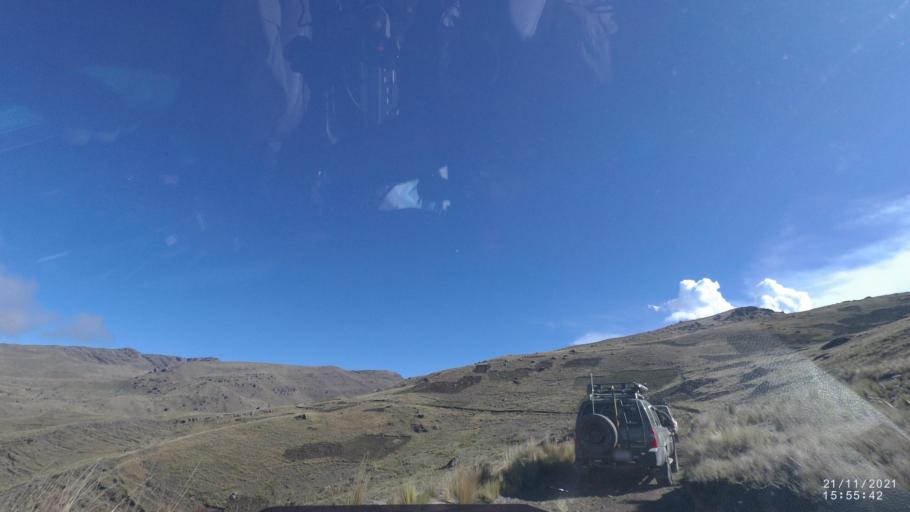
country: BO
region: Cochabamba
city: Cochabamba
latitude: -16.9739
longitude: -66.2658
